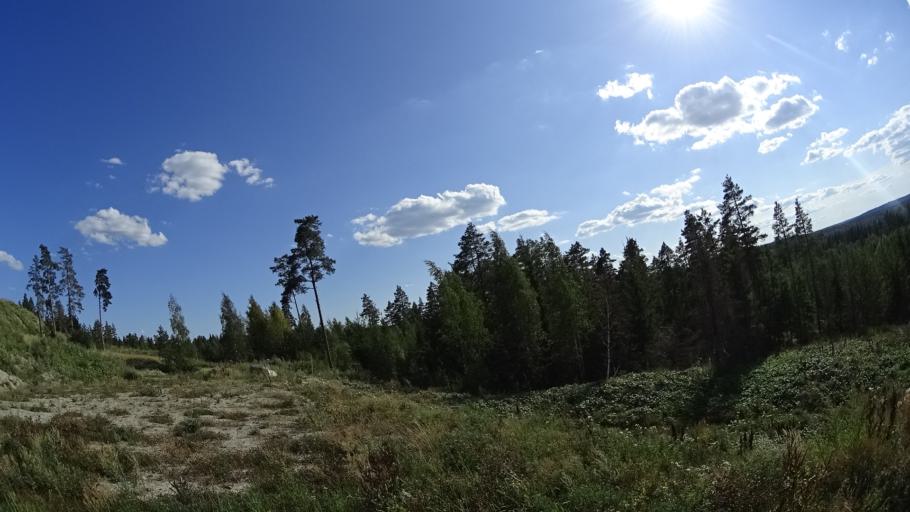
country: FI
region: Uusimaa
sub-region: Helsinki
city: Vihti
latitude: 60.3762
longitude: 24.3658
